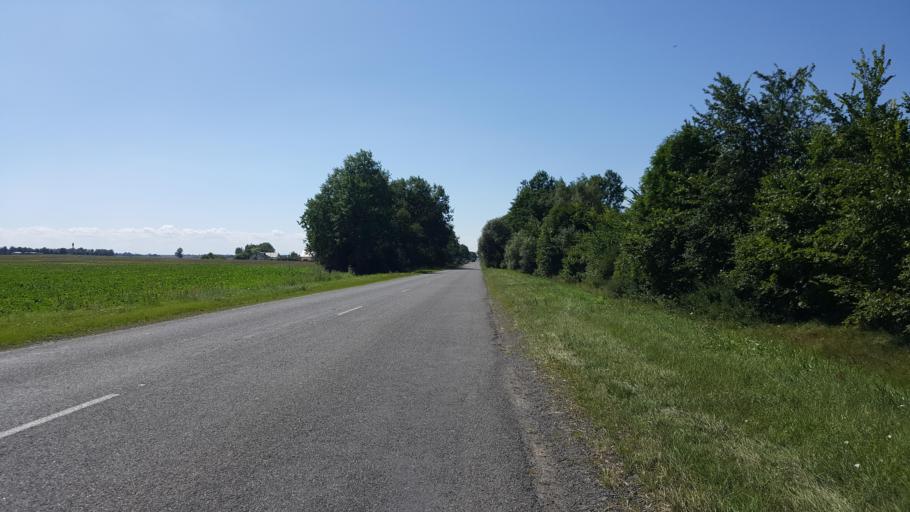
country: BY
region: Brest
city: Charnawchytsy
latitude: 52.2053
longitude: 23.7699
